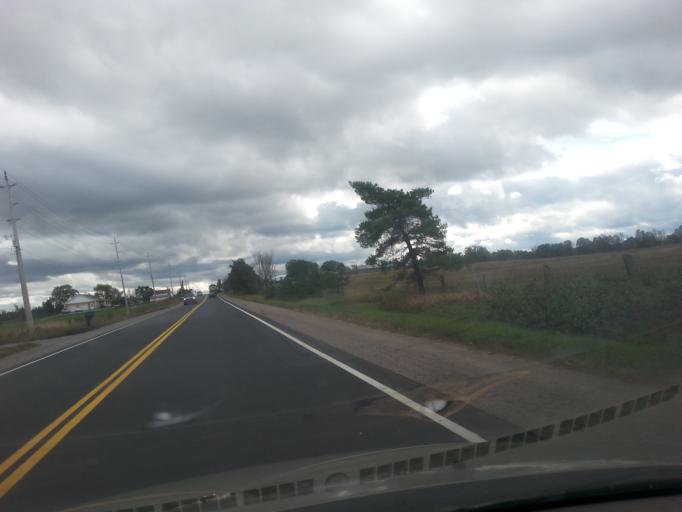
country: CA
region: Ontario
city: Pembroke
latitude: 45.5614
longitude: -77.1164
